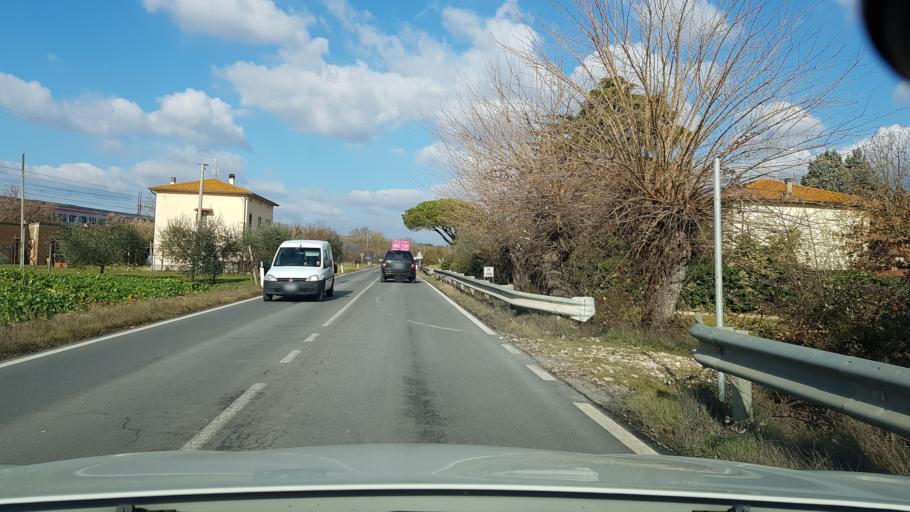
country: IT
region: Umbria
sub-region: Provincia di Perugia
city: Castiglione del Lago
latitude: 43.1535
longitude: 12.0197
